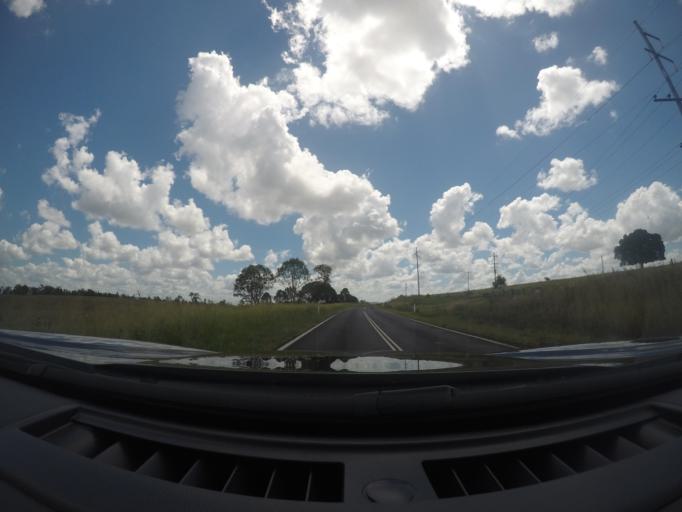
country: AU
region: Queensland
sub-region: Moreton Bay
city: Woodford
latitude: -27.1416
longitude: 152.4993
